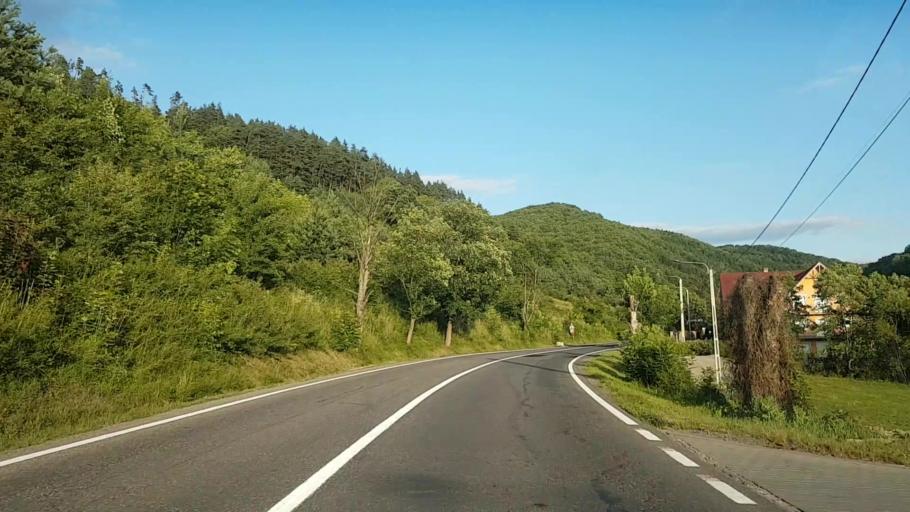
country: RO
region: Harghita
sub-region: Comuna Corund
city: Corund
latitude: 46.4665
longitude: 25.2037
